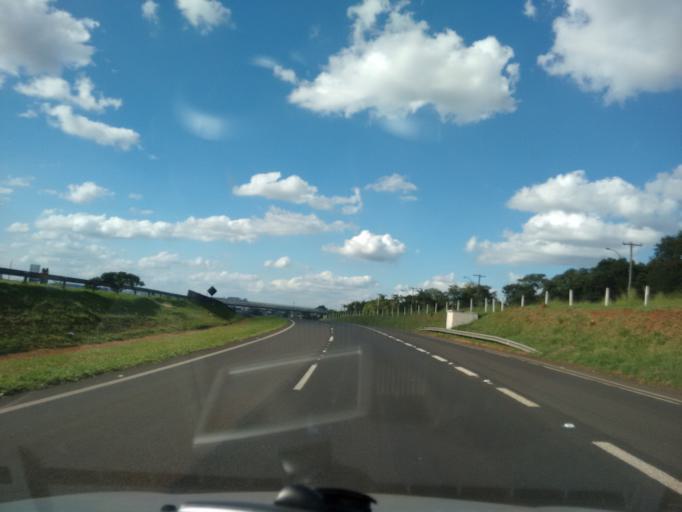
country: BR
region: Sao Paulo
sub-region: Araraquara
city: Araraquara
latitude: -21.8120
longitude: -48.1558
